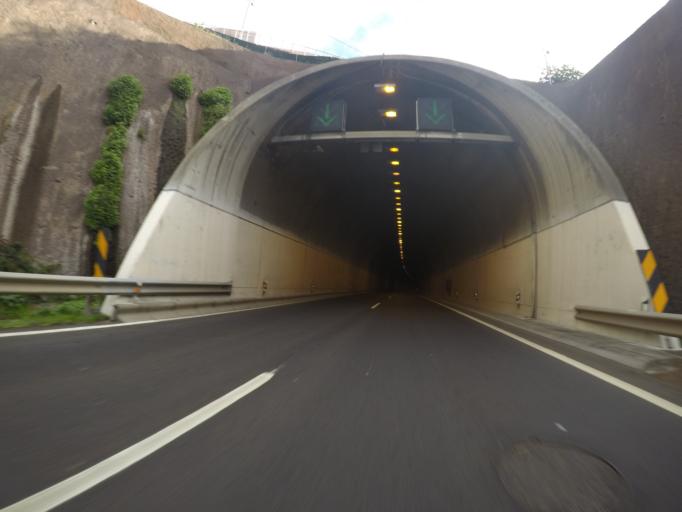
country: PT
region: Madeira
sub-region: Funchal
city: Nossa Senhora do Monte
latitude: 32.6617
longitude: -16.9269
